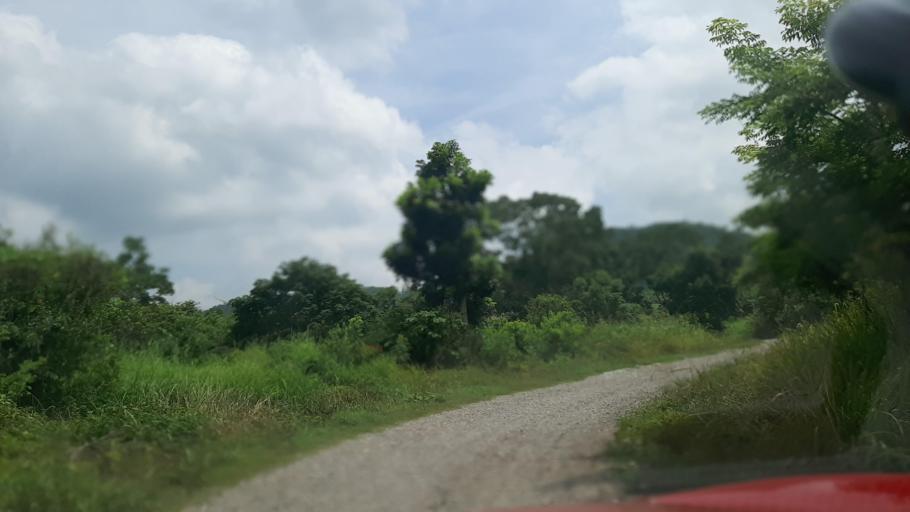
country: MX
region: Veracruz
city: Gutierrez Zamora
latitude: 20.4471
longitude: -97.1759
